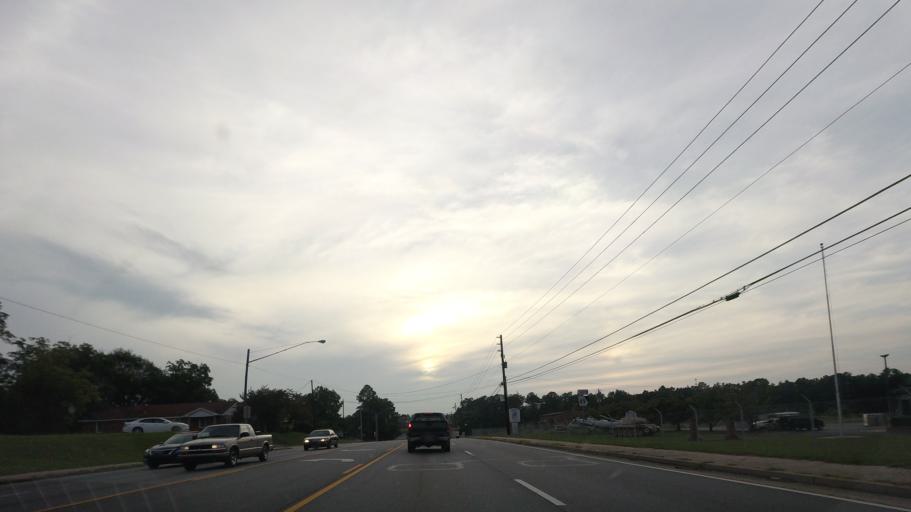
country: US
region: Georgia
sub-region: Bibb County
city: Macon
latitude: 32.8596
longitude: -83.6061
